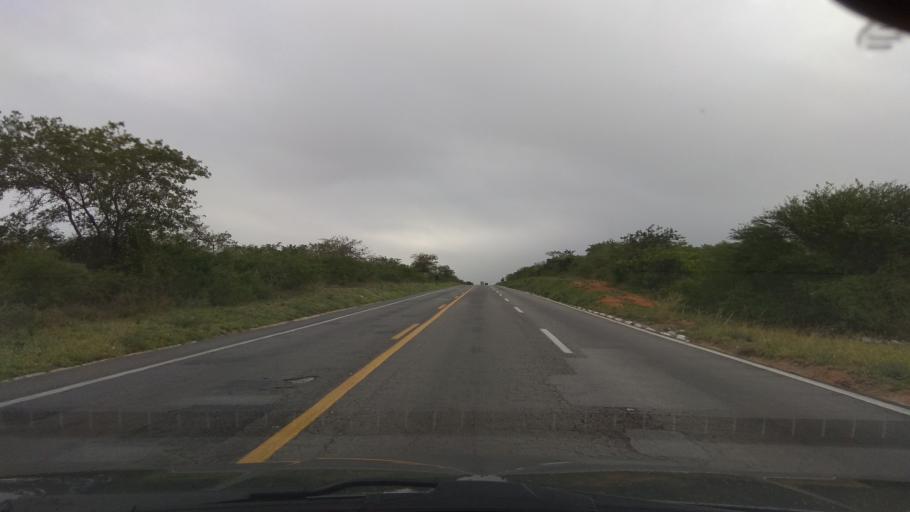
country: BR
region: Bahia
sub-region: Santa Ines
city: Santa Ines
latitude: -13.0301
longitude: -39.9628
